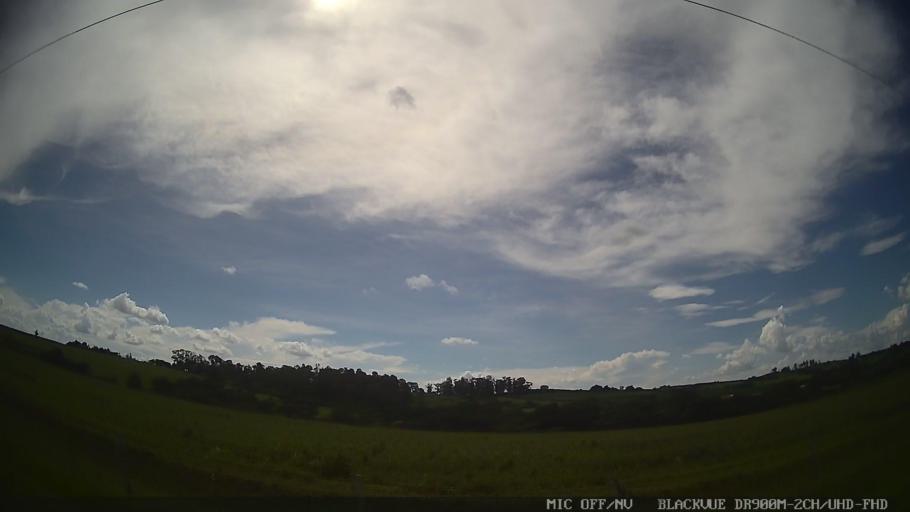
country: BR
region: Sao Paulo
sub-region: Conchas
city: Conchas
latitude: -22.9653
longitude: -47.9832
